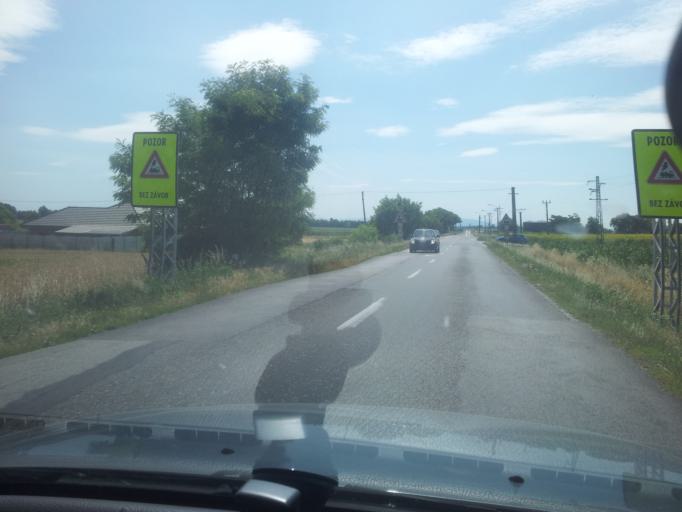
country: SK
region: Nitriansky
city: Levice
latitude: 48.1638
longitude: 18.5512
